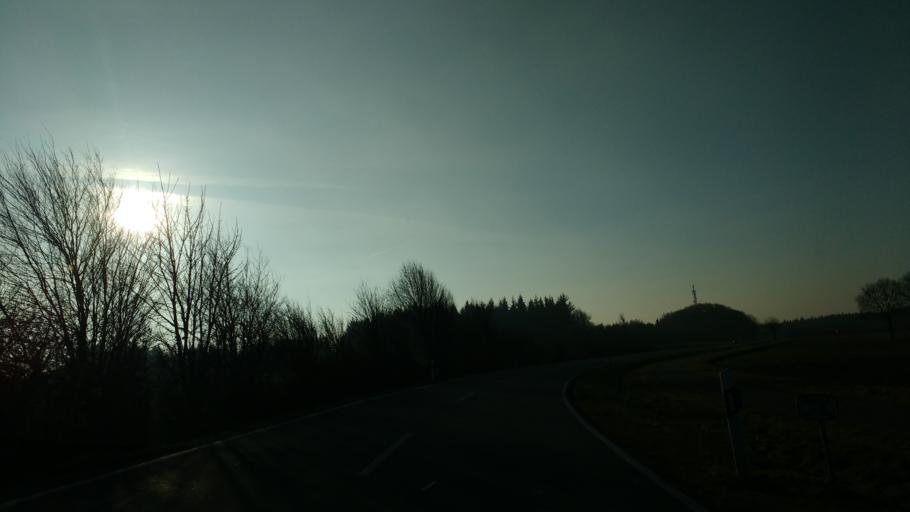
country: DE
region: Schleswig-Holstein
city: Nindorf
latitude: 54.1203
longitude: 9.7010
